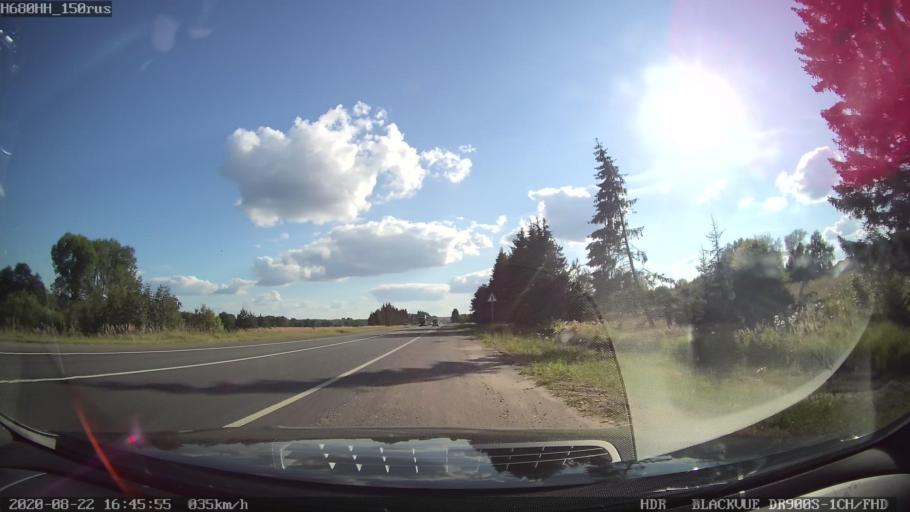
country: RU
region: Tverskaya
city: Rameshki
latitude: 57.2868
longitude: 36.0878
